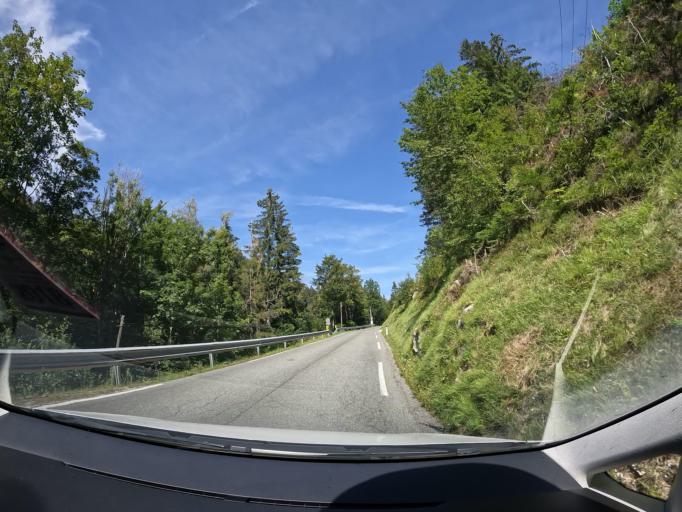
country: AT
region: Carinthia
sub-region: Politischer Bezirk Villach Land
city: Sankt Jakob
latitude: 46.5584
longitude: 14.0772
